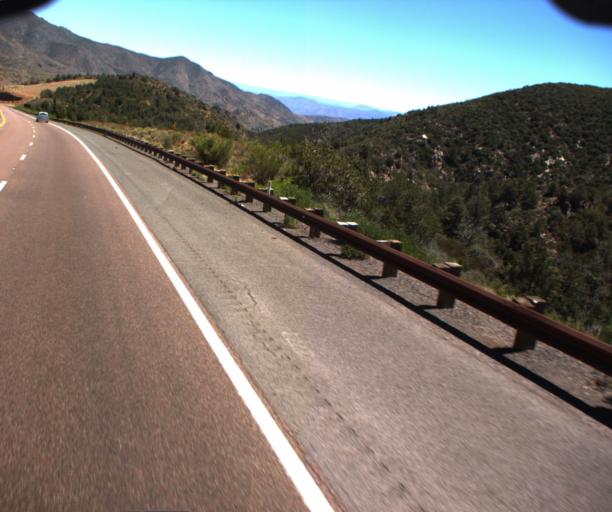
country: US
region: Arizona
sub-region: Gila County
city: Tonto Basin
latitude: 33.9300
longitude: -111.4429
